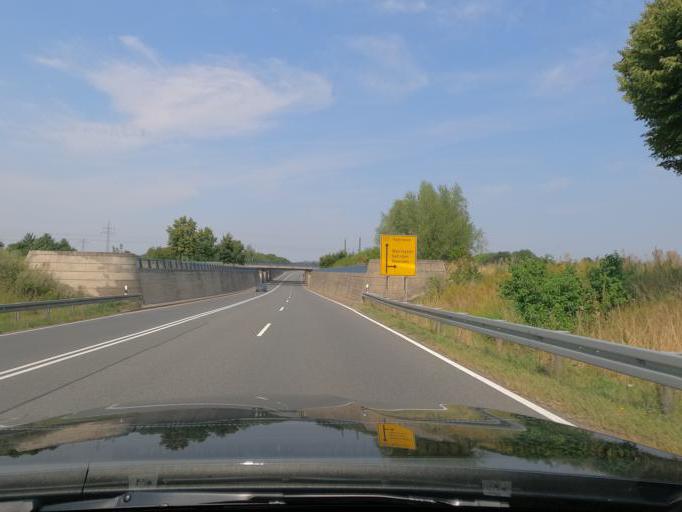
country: DE
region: Lower Saxony
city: Gehrden
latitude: 52.2913
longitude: 9.6300
